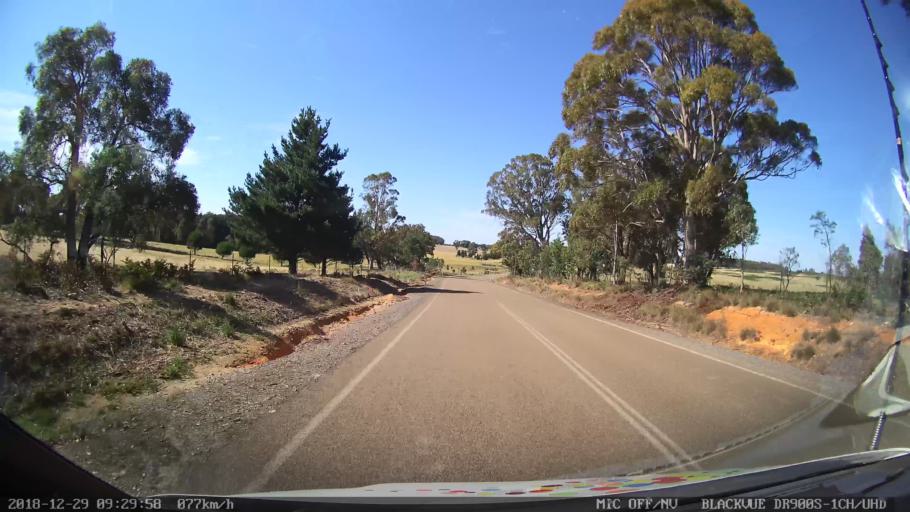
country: AU
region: New South Wales
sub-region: Upper Lachlan Shire
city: Crookwell
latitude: -34.5936
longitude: 149.3721
